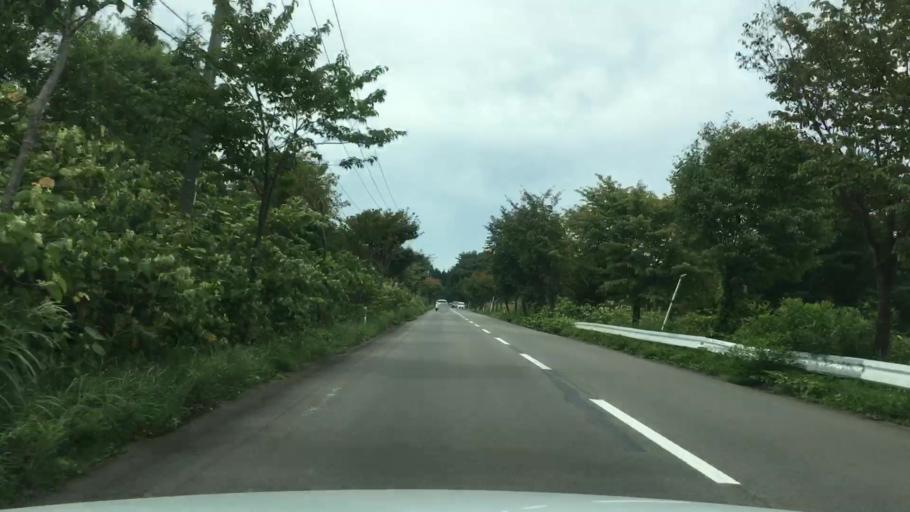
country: JP
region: Aomori
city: Shimokizukuri
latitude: 40.7122
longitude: 140.2854
